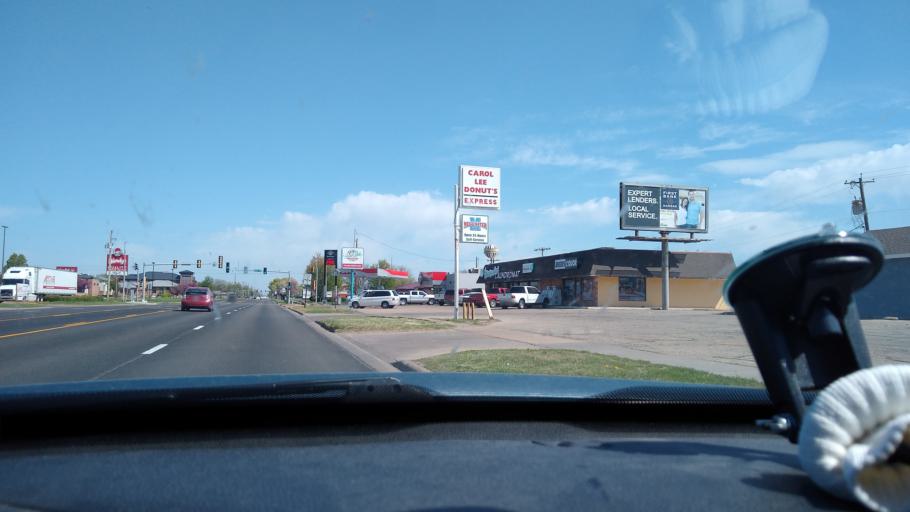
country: US
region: Kansas
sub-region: Saline County
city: Salina
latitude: 38.8077
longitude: -97.5942
